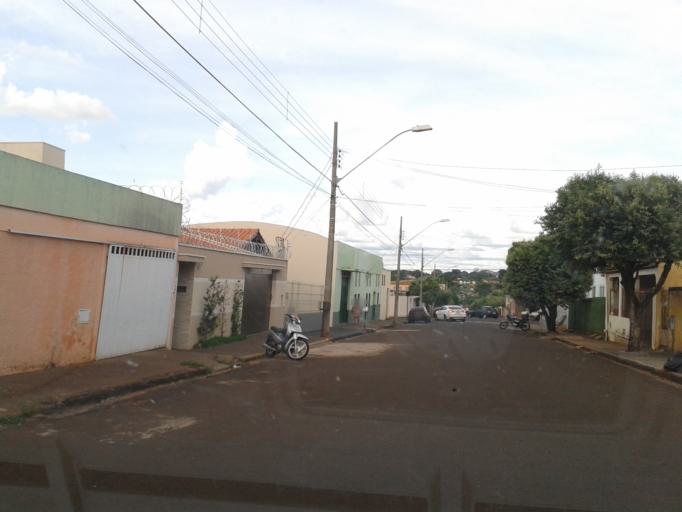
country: BR
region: Minas Gerais
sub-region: Ituiutaba
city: Ituiutaba
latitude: -18.9764
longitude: -49.4547
